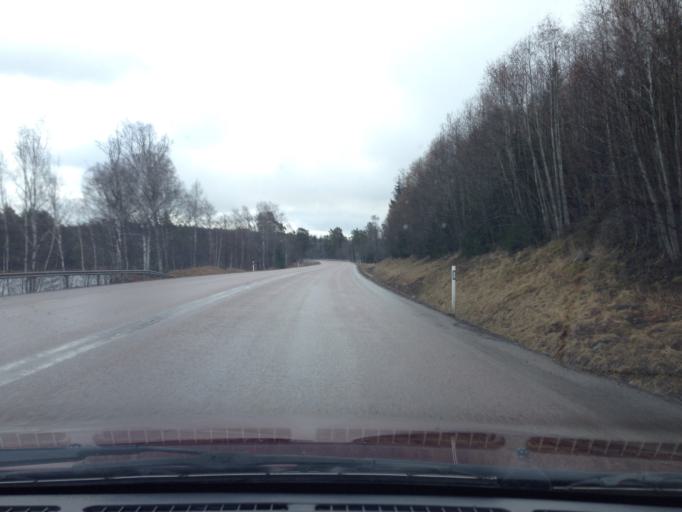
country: SE
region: Dalarna
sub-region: Ludvika Kommun
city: Ludvika
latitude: 60.1560
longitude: 15.2414
